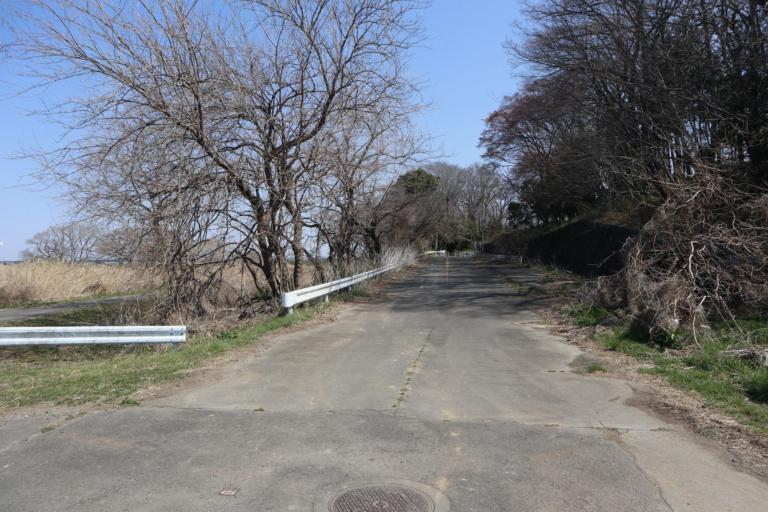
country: JP
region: Ibaraki
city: Koga
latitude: 36.2352
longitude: 139.7156
